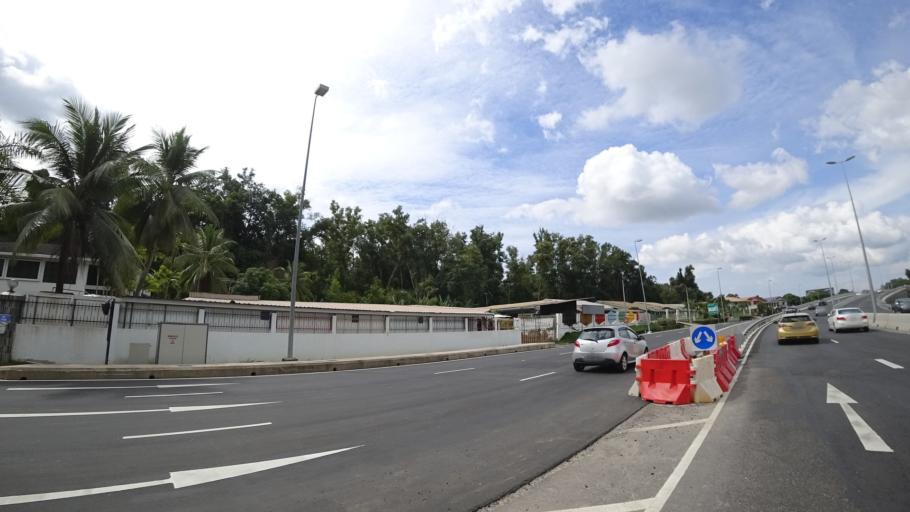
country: BN
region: Brunei and Muara
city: Bandar Seri Begawan
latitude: 4.8815
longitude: 114.8902
